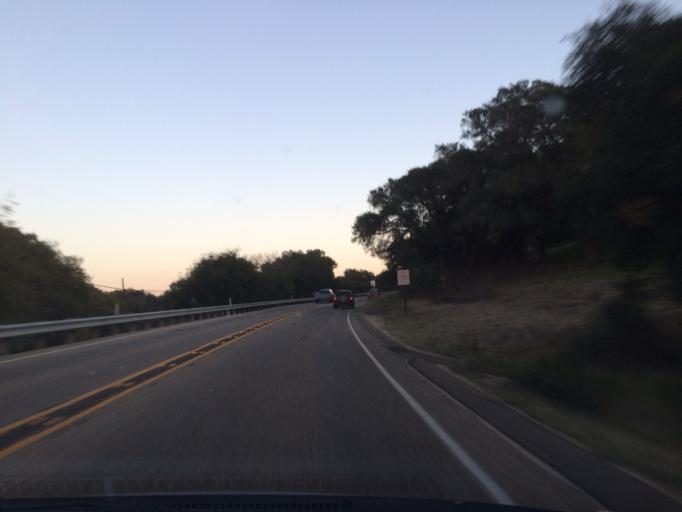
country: US
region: California
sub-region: Santa Barbara County
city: Santa Ynez
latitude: 34.5847
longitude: -119.9940
